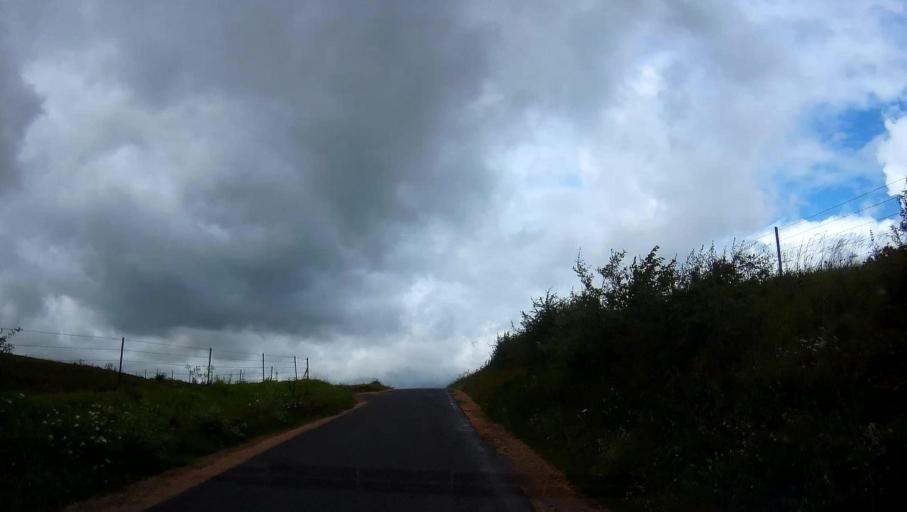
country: FR
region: Champagne-Ardenne
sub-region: Departement des Ardennes
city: Rimogne
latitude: 49.7564
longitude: 4.5374
